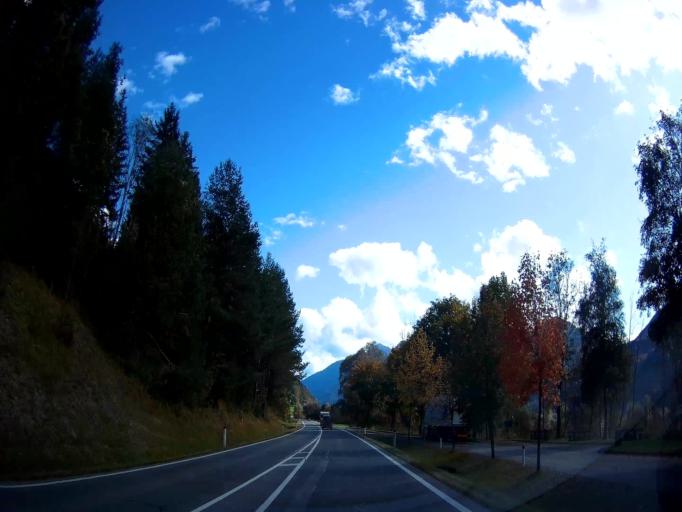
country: AT
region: Carinthia
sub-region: Politischer Bezirk Spittal an der Drau
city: Oberdrauburg
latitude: 46.7550
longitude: 12.9508
